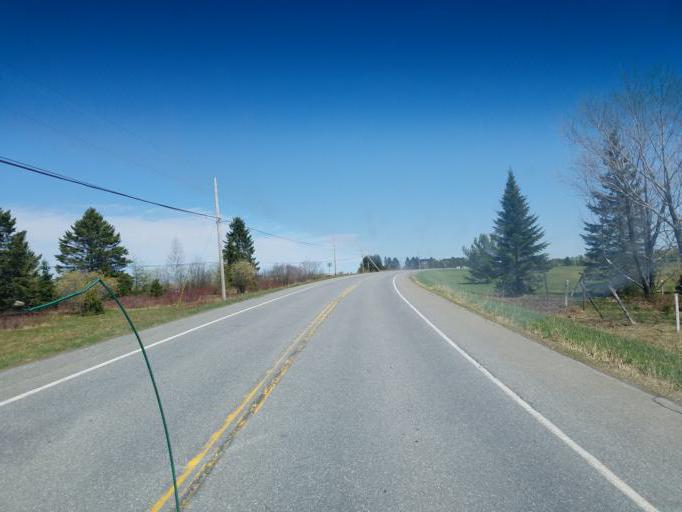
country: US
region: Maine
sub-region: Aroostook County
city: Caribou
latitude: 46.8438
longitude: -68.0626
